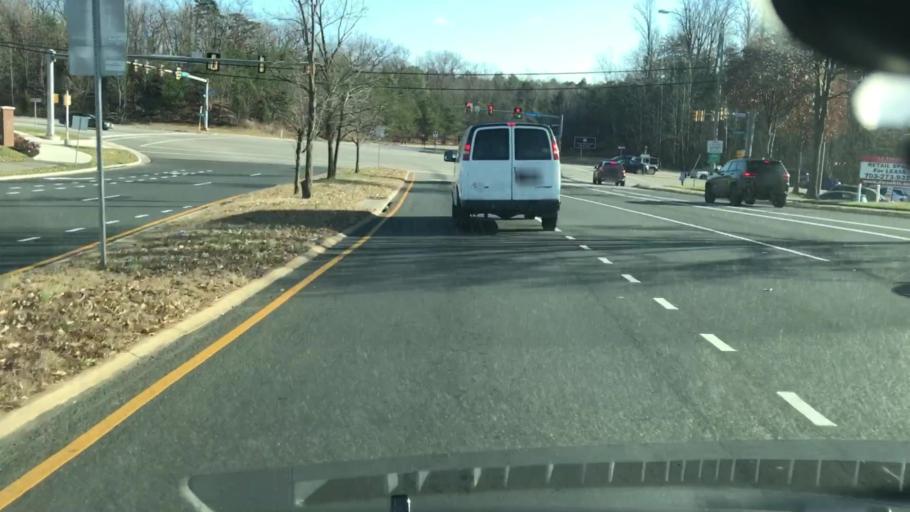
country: US
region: Virginia
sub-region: Fairfax County
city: Newington
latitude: 38.7409
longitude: -77.1638
